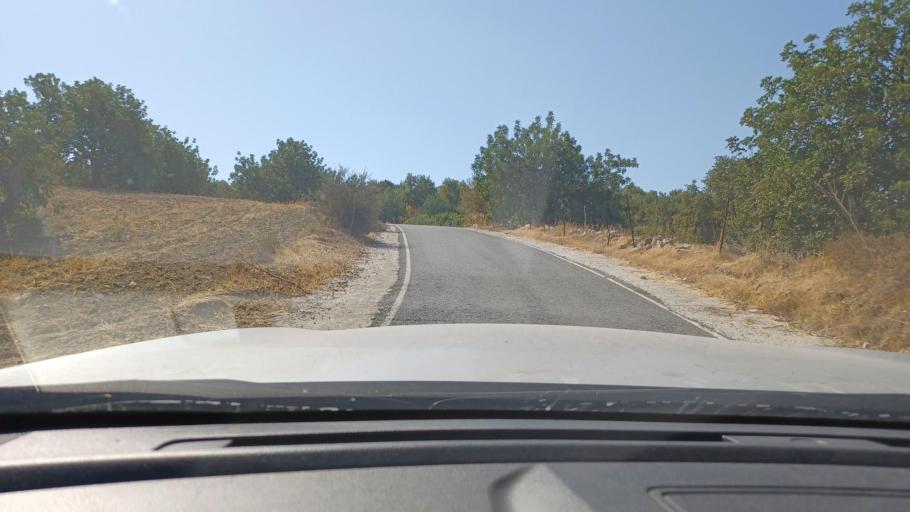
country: CY
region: Pafos
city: Polis
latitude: 34.9978
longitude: 32.4979
